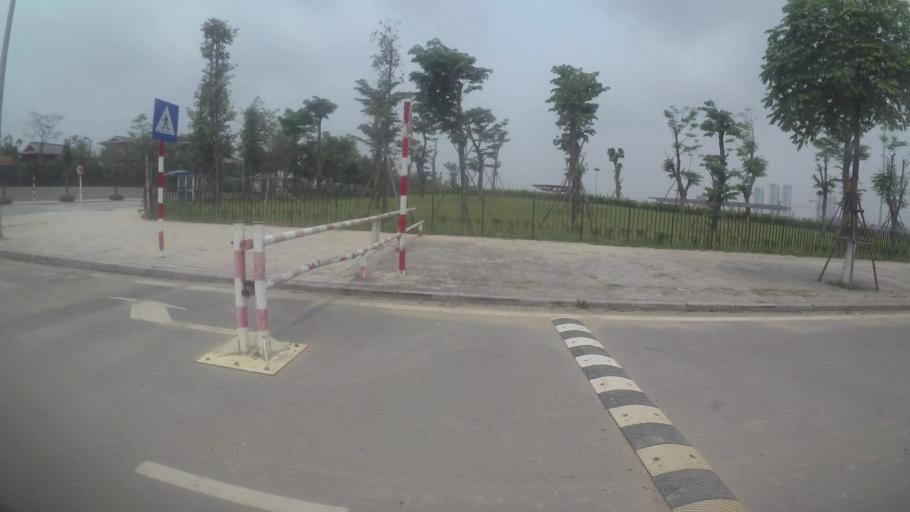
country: VN
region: Ha Noi
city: Ha Dong
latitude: 20.9786
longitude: 105.7587
